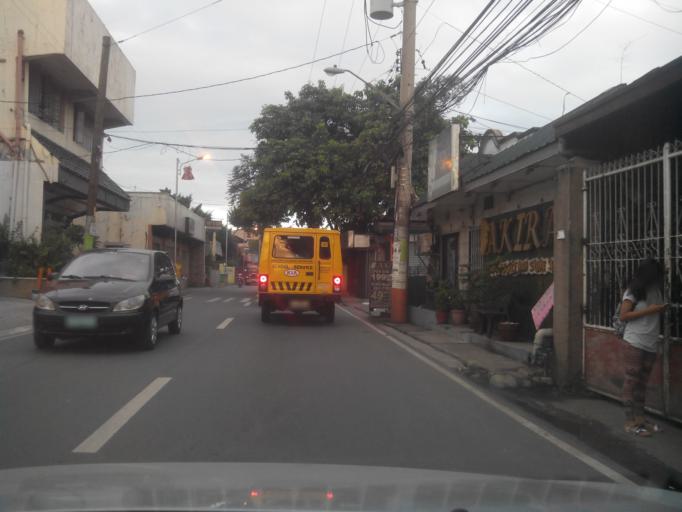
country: PH
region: Calabarzon
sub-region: Province of Rizal
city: Cainta
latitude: 14.5723
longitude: 121.1272
